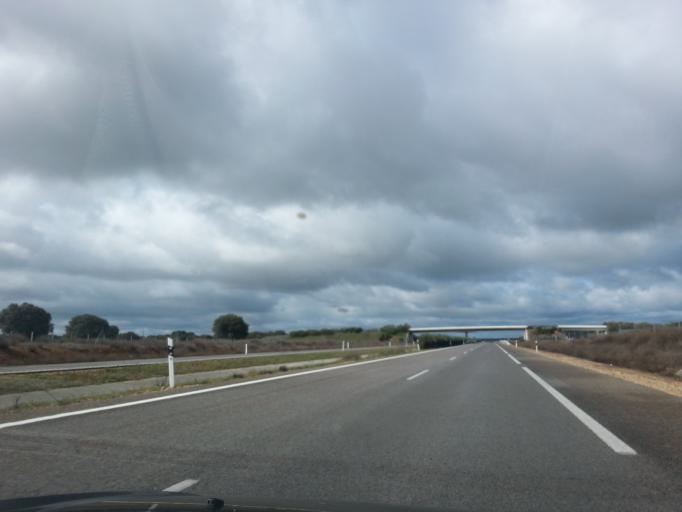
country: ES
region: Castille and Leon
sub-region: Provincia de Salamanca
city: San Munoz
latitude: 40.8079
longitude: -6.1784
